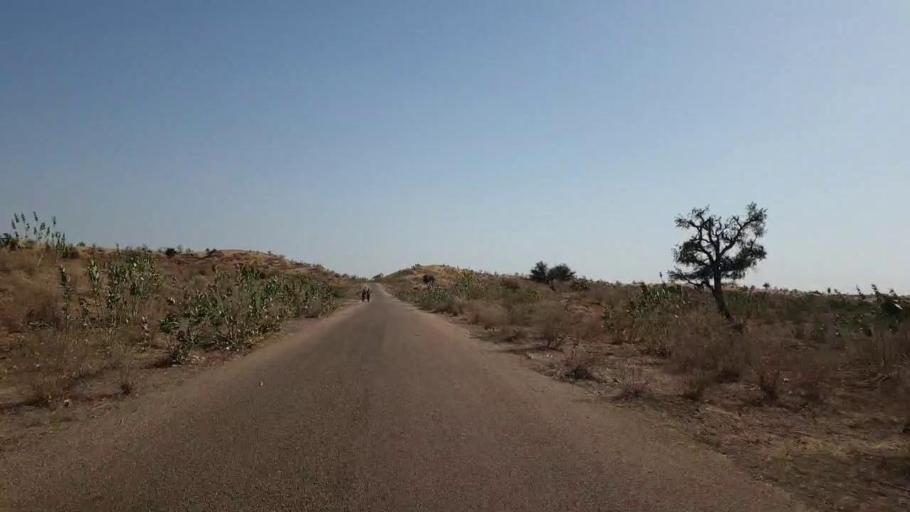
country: PK
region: Sindh
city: Umarkot
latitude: 25.1088
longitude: 70.0378
